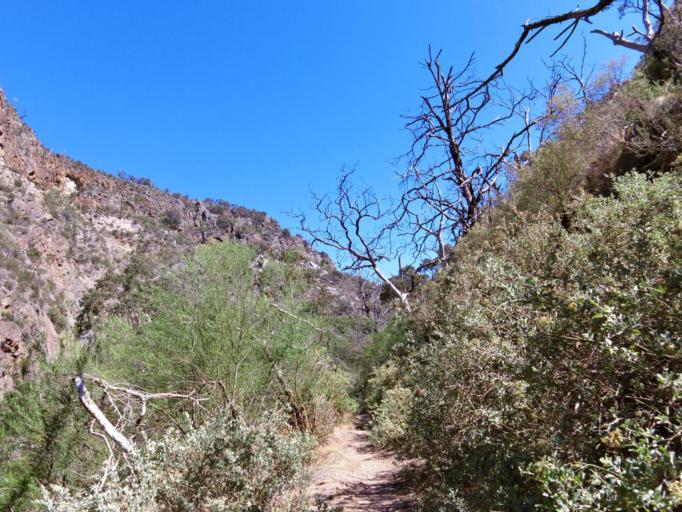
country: AU
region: Victoria
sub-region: Moorabool
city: Bacchus Marsh
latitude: -37.6668
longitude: 144.3547
